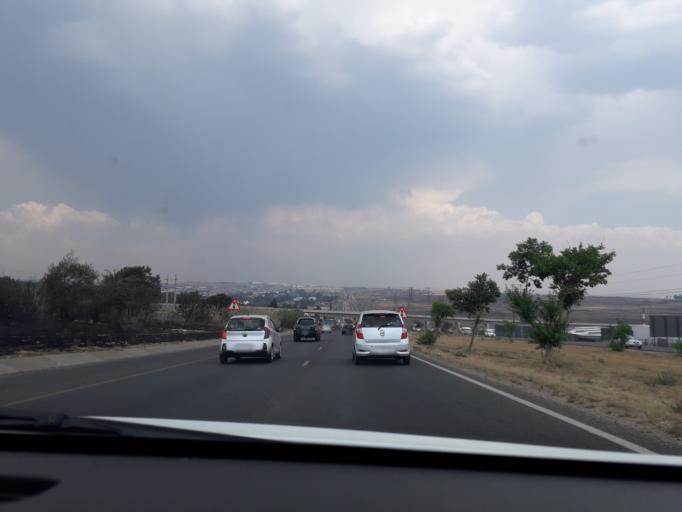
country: ZA
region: Gauteng
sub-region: City of Johannesburg Metropolitan Municipality
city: Midrand
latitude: -26.0206
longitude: 28.1246
